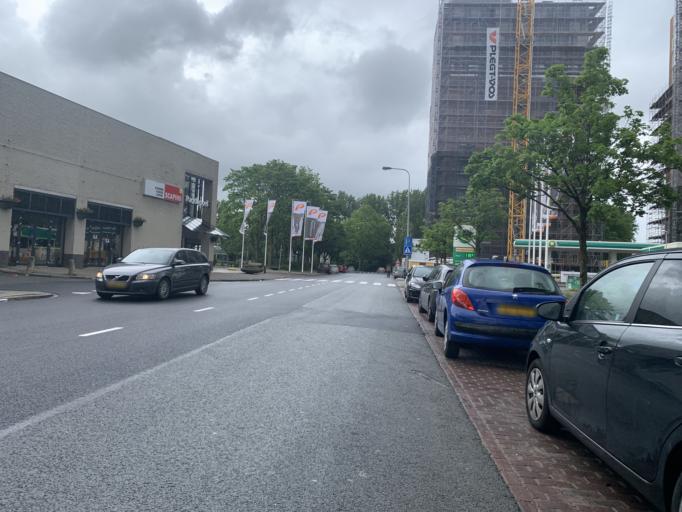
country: NL
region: Groningen
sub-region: Gemeente Groningen
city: Korrewegwijk
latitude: 53.2291
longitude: 6.5442
